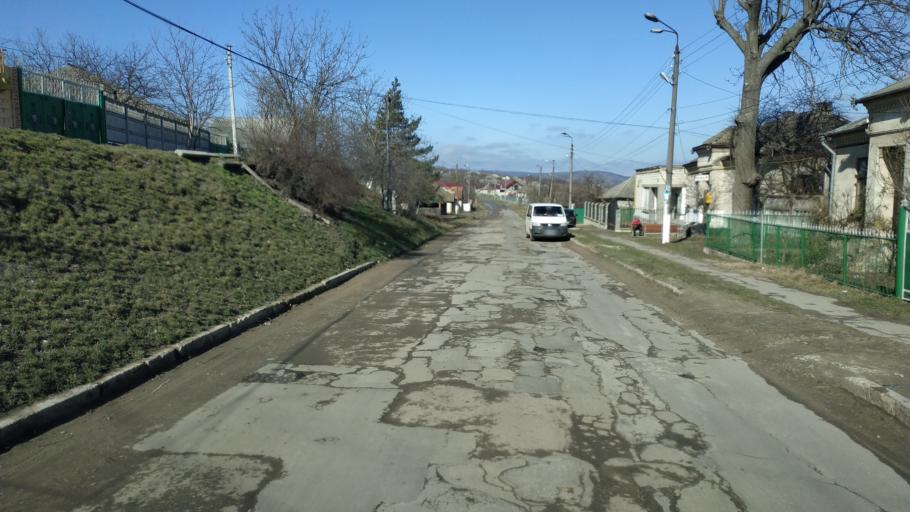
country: MD
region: Hincesti
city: Hincesti
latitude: 46.9695
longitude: 28.5893
